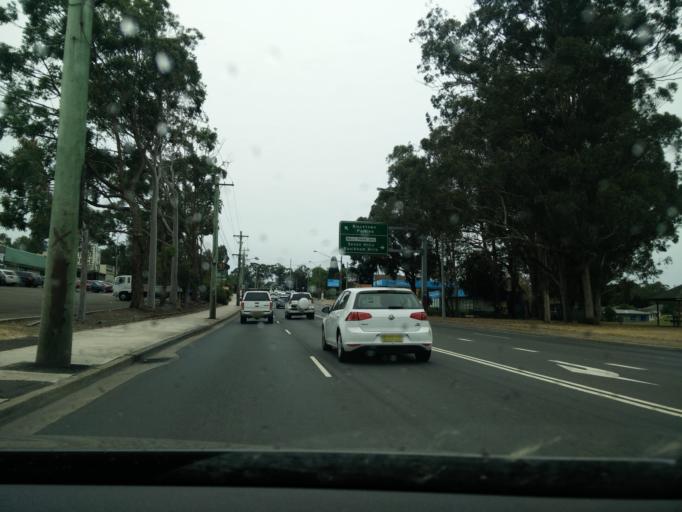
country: AU
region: New South Wales
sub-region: Blacktown
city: Blacktown
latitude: -33.7789
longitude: 150.9203
